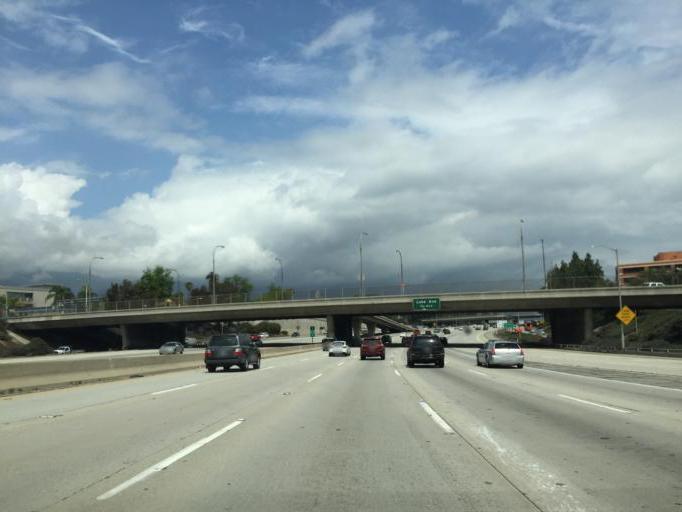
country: US
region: California
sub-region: Los Angeles County
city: Pasadena
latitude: 34.1513
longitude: -118.1516
